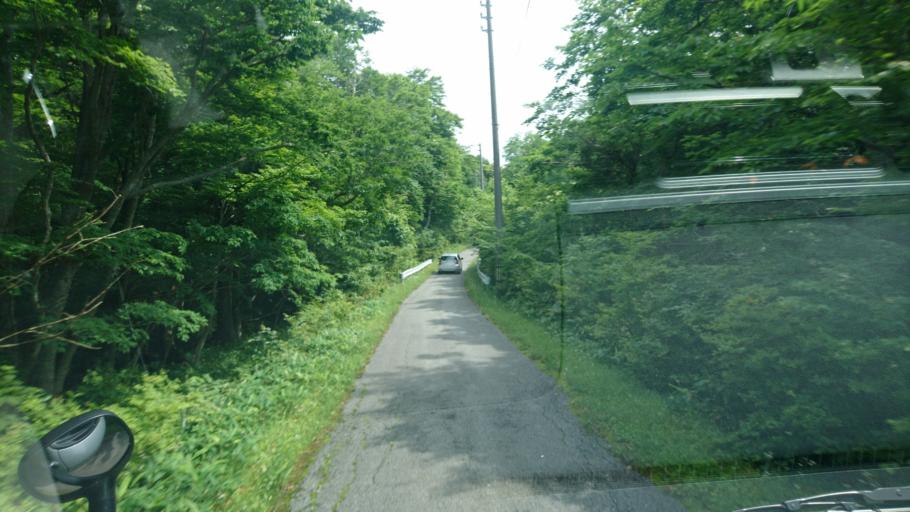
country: JP
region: Iwate
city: Ofunato
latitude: 39.1643
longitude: 141.7487
